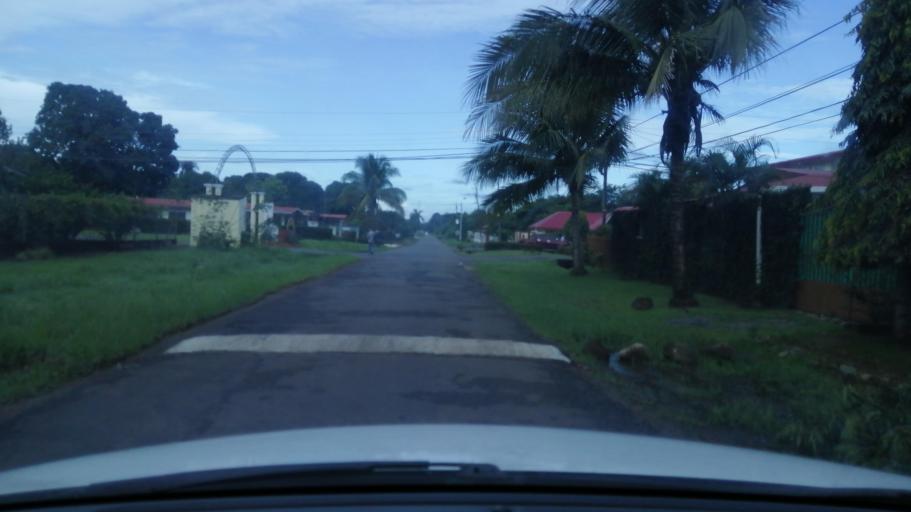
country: PA
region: Chiriqui
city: El Quiteno
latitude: 8.4684
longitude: -82.4132
